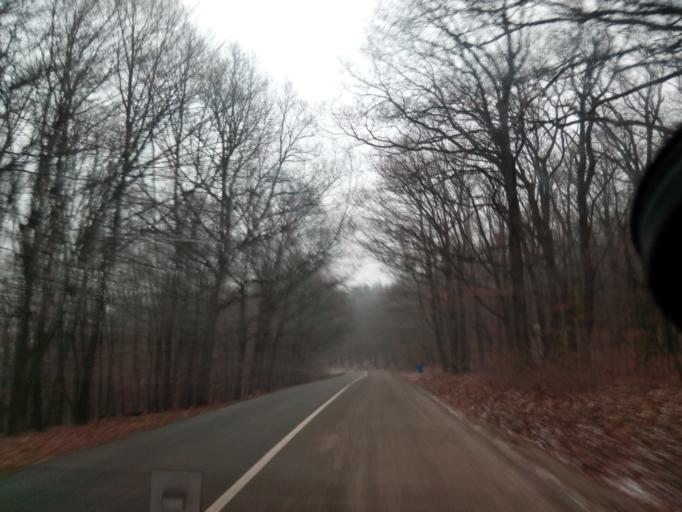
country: SK
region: Kosicky
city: Kosice
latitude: 48.7104
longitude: 21.1855
